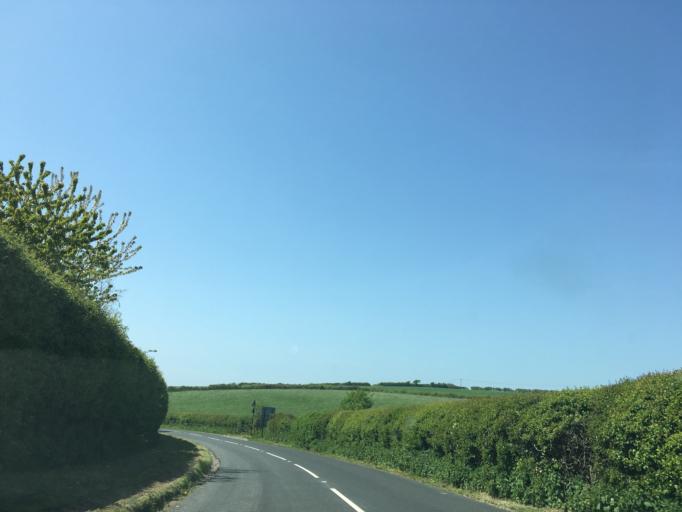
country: GB
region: England
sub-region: Isle of Wight
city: Niton
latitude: 50.5919
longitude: -1.2468
